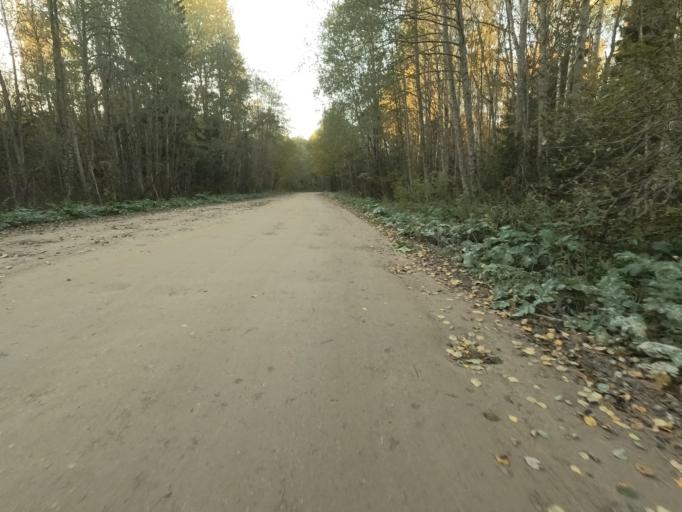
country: RU
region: Leningrad
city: Lyuban'
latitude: 59.0059
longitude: 31.0941
